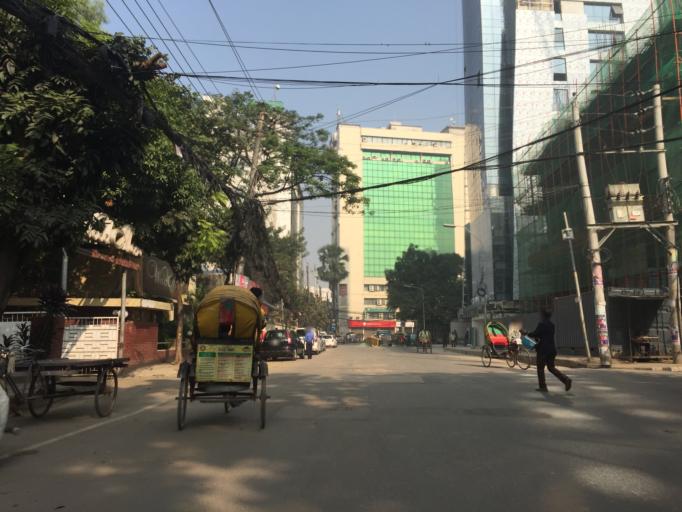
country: BD
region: Dhaka
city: Paltan
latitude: 23.7932
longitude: 90.4131
